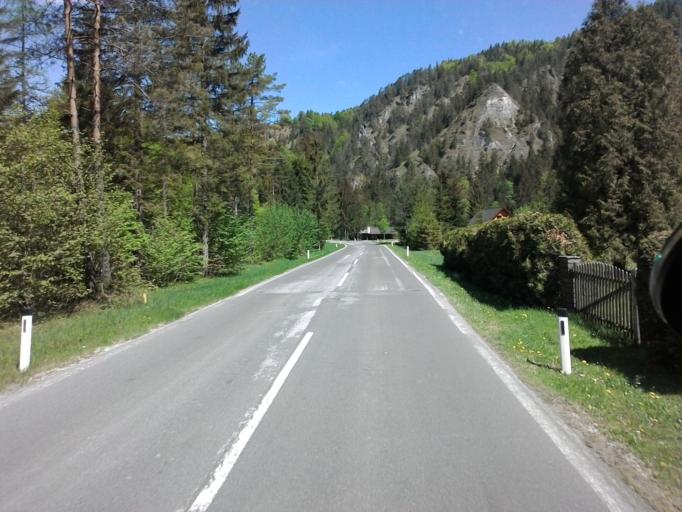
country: AT
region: Styria
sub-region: Politischer Bezirk Liezen
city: Wildalpen
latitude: 47.6672
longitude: 14.9792
